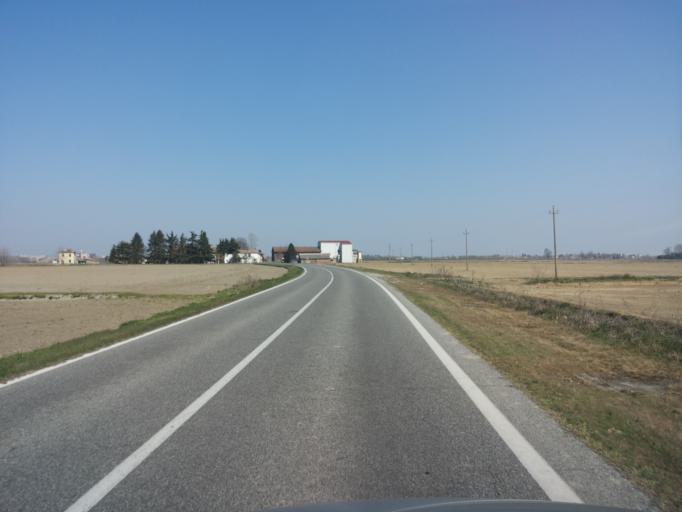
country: IT
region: Piedmont
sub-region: Provincia di Vercelli
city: Asigliano Vercellese
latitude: 45.2824
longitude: 8.4234
